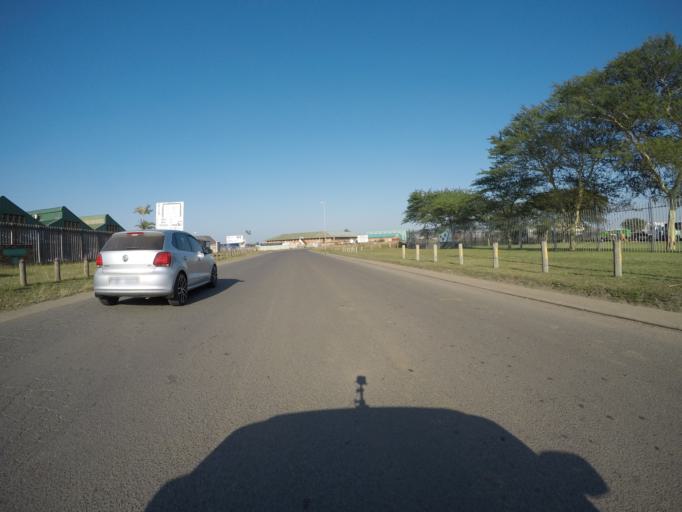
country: ZA
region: KwaZulu-Natal
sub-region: uThungulu District Municipality
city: Richards Bay
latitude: -28.7504
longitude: 32.0291
